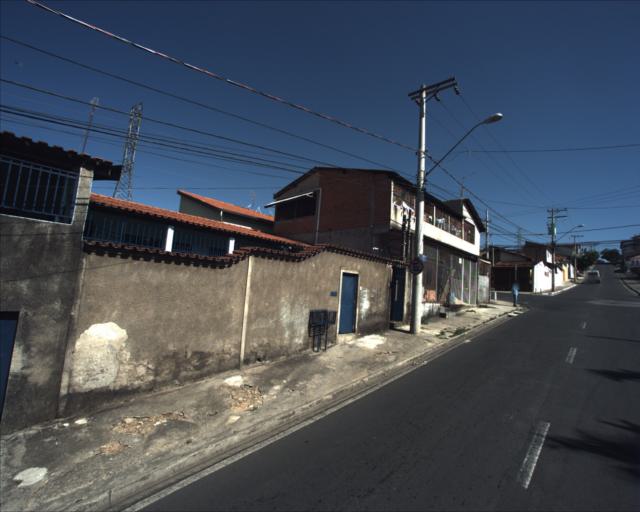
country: BR
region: Sao Paulo
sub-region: Sorocaba
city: Sorocaba
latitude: -23.5038
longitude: -47.5075
